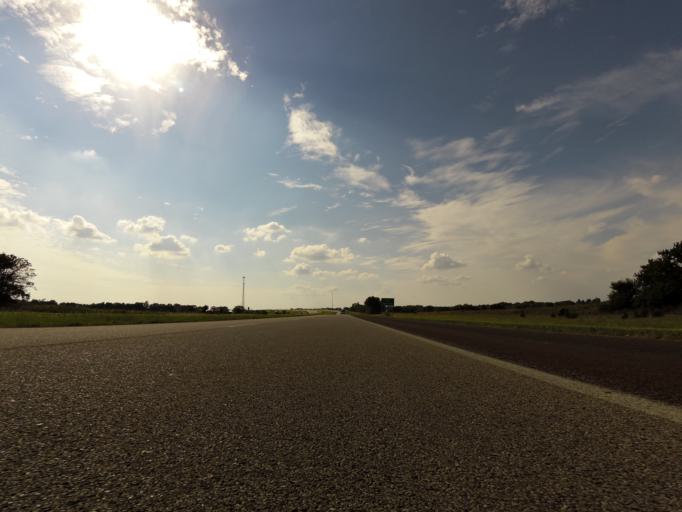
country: US
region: Kansas
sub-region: Reno County
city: Haven
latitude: 37.9333
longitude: -97.8566
